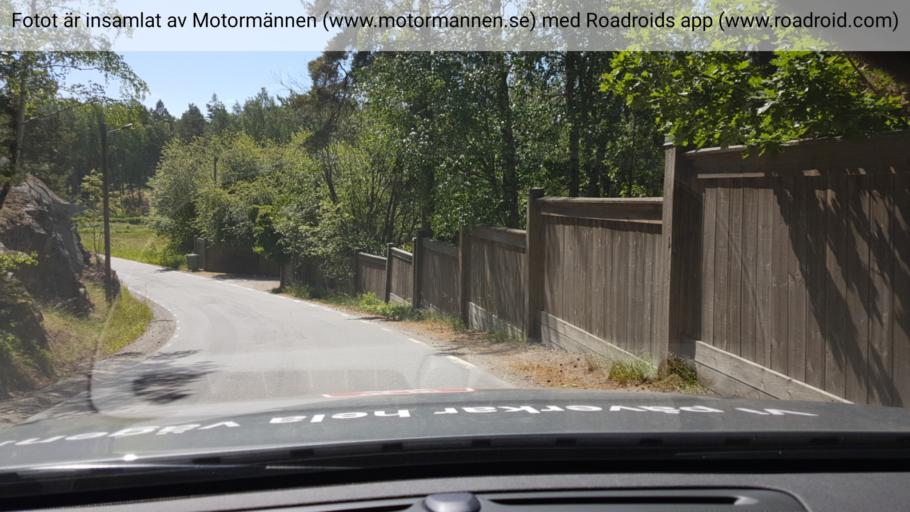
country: SE
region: Stockholm
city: Dalaro
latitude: 59.1498
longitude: 18.4329
